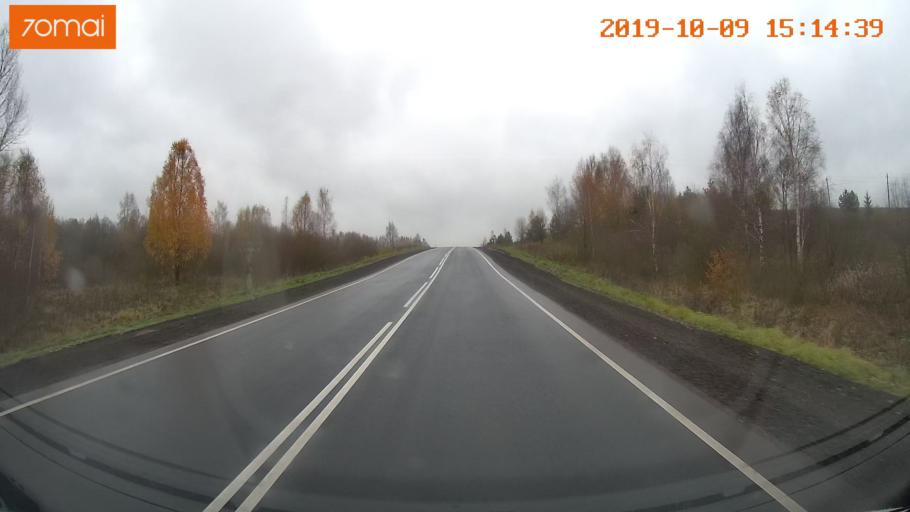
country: RU
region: Kostroma
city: Susanino
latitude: 58.1315
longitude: 41.6012
